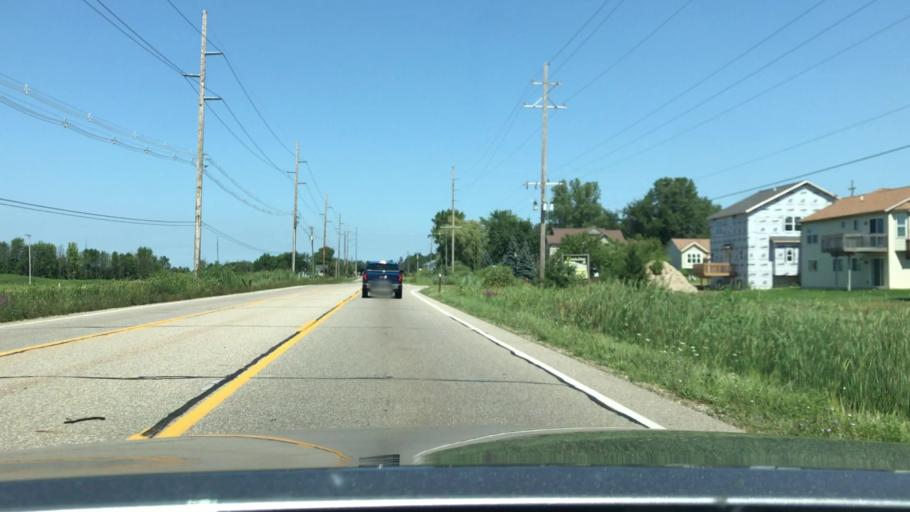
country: US
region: Michigan
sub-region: Ottawa County
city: Holland
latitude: 42.8363
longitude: -86.0788
